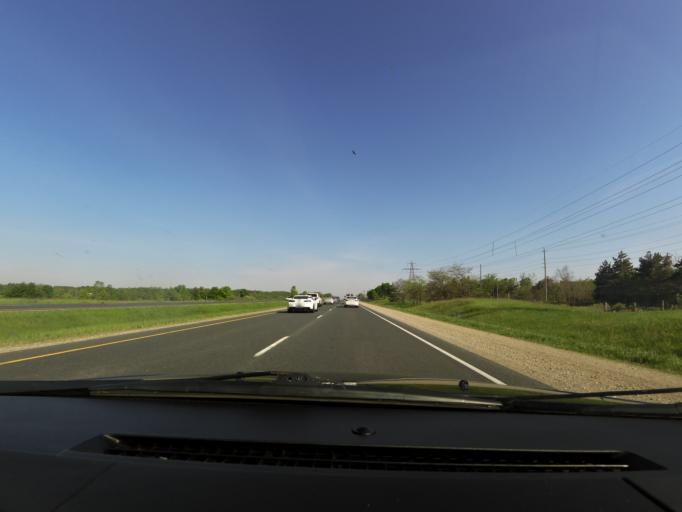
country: CA
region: Ontario
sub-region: Wellington County
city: Guelph
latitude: 43.4746
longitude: -80.1910
